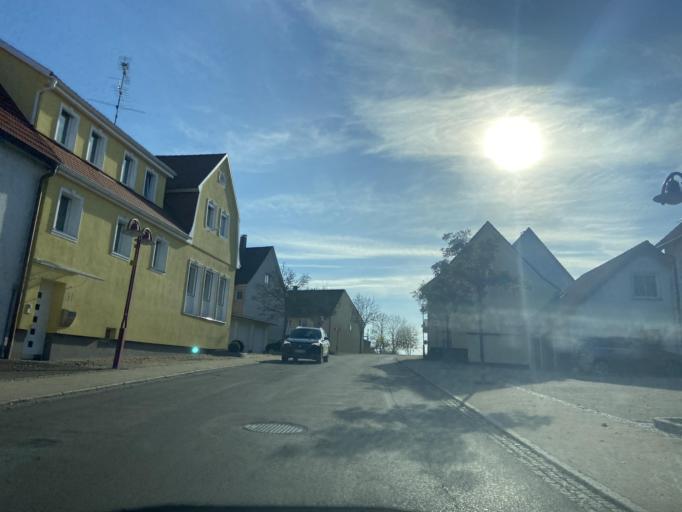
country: DE
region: Baden-Wuerttemberg
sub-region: Tuebingen Region
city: Stetten am Kalten Markt
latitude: 48.1194
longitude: 9.0813
